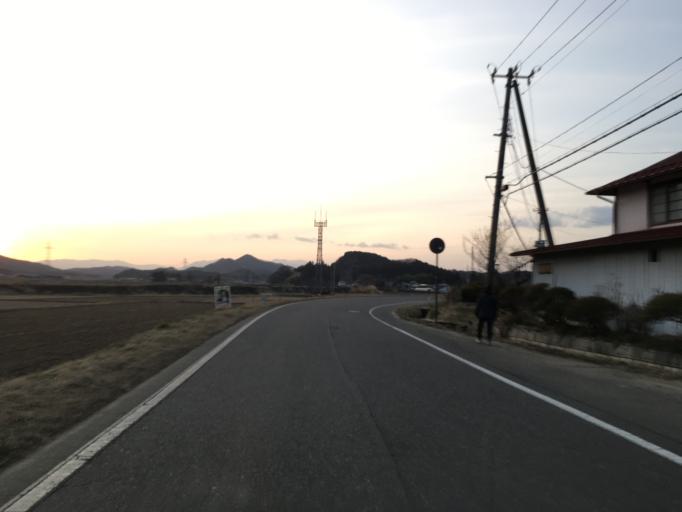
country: JP
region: Fukushima
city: Ishikawa
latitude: 37.0683
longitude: 140.3108
